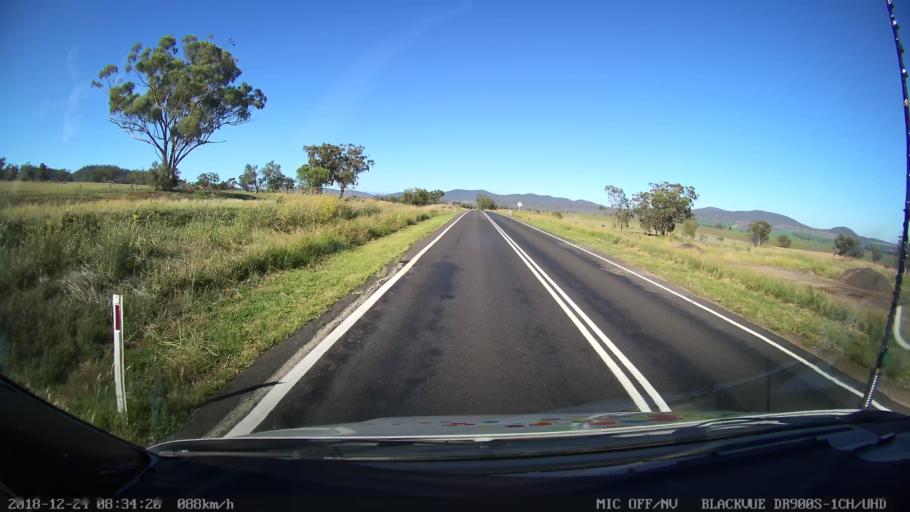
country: AU
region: New South Wales
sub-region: Liverpool Plains
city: Quirindi
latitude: -31.2921
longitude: 150.6722
